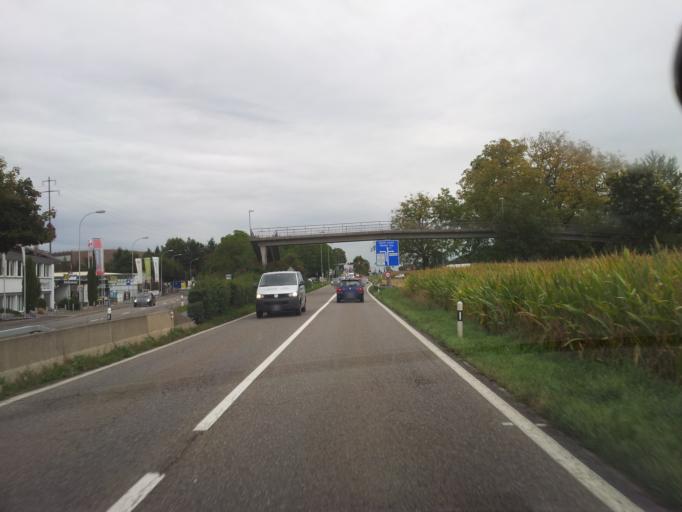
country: CH
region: Aargau
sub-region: Bezirk Bremgarten
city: Villmergen
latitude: 47.3536
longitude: 8.2509
